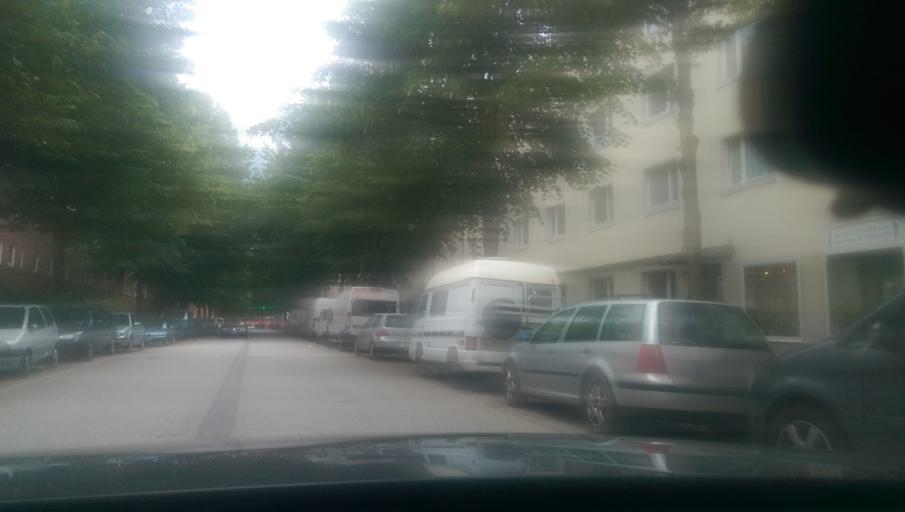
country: DE
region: Hamburg
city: Kleiner Grasbrook
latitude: 53.5124
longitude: 9.9870
